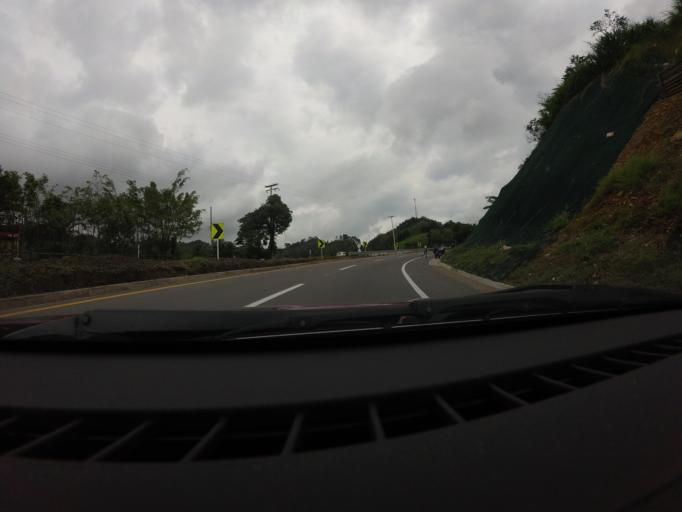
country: CO
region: Cundinamarca
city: San Francisco
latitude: 4.9755
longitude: -74.3102
